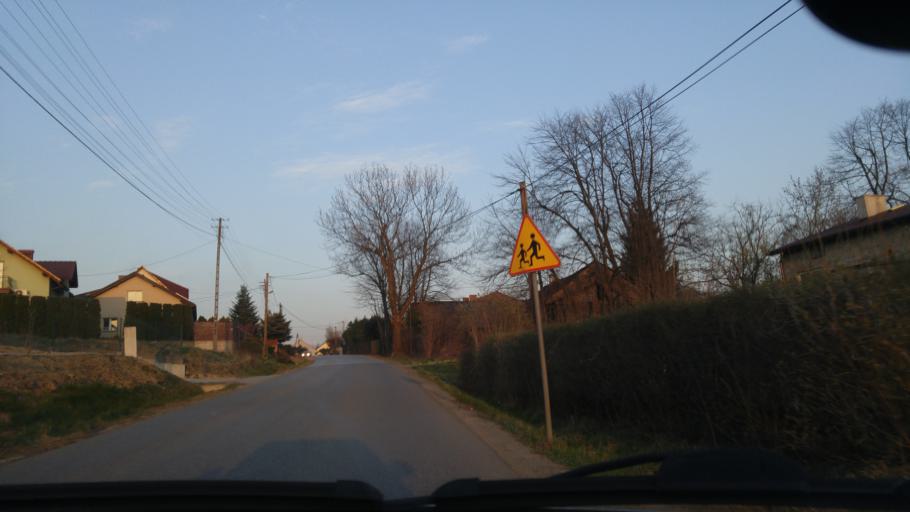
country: PL
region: Lesser Poland Voivodeship
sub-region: Powiat krakowski
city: Radziszow
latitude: 49.9464
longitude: 19.8445
